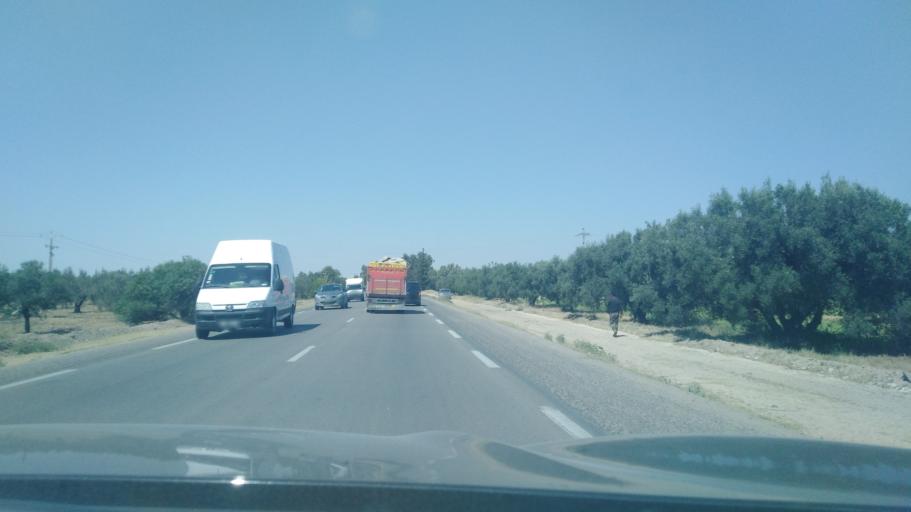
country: TN
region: Al Qayrawan
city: Kairouan
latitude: 35.6100
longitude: 9.9107
